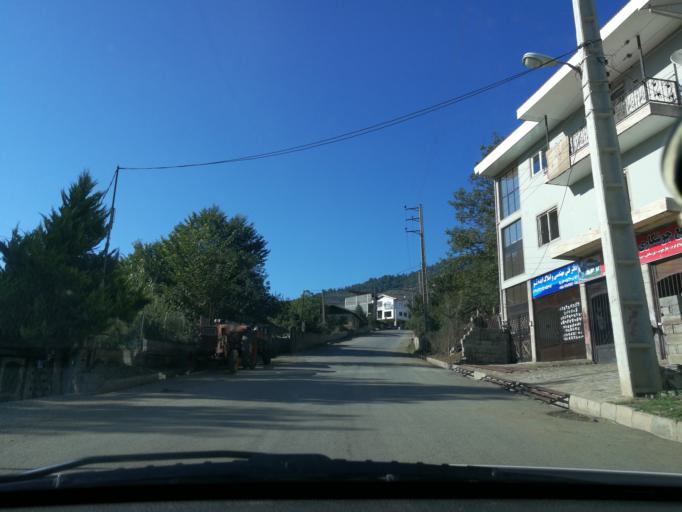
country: IR
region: Mazandaran
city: `Abbasabad
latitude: 36.5510
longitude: 51.1895
